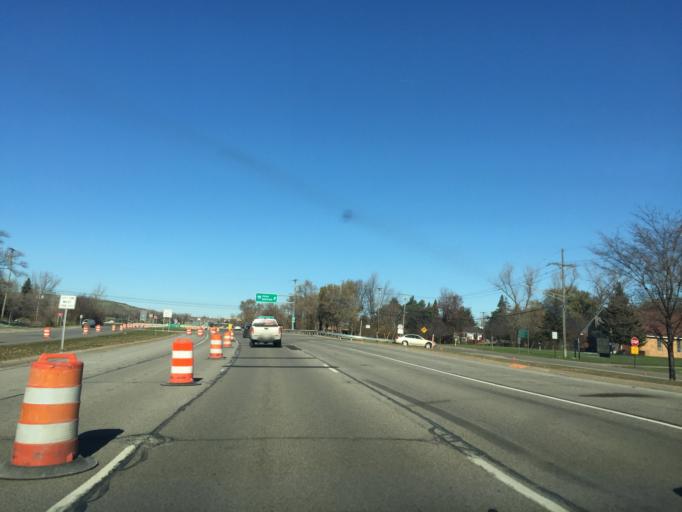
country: US
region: Michigan
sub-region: Oakland County
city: Auburn Hills
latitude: 42.6879
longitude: -83.2408
